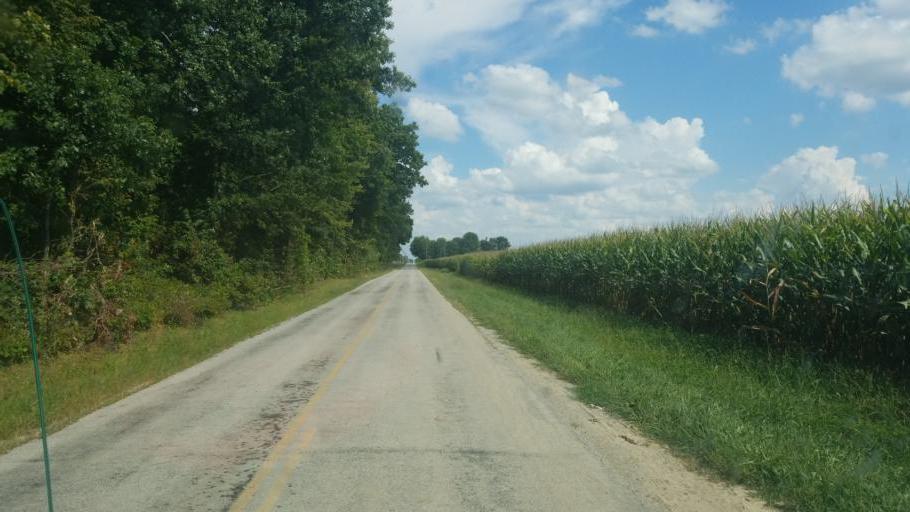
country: US
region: Ohio
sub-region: Seneca County
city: Tiffin
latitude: 40.9933
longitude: -83.1359
